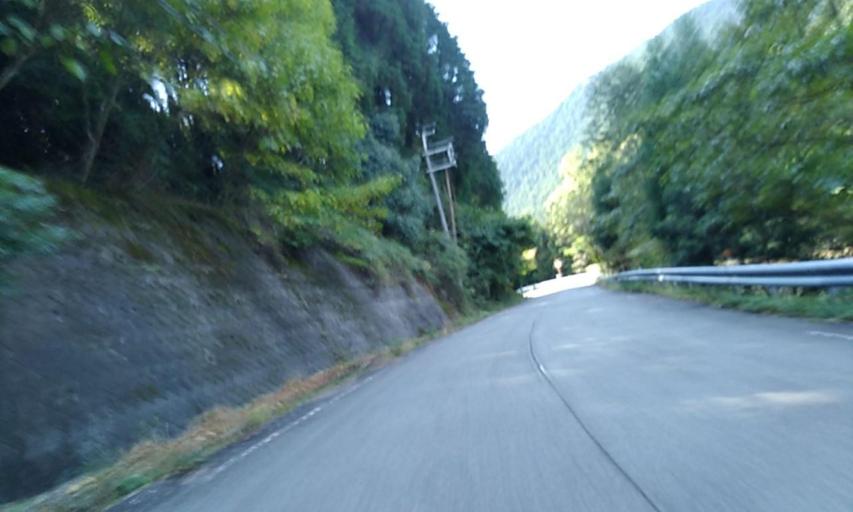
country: JP
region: Wakayama
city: Iwade
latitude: 34.1133
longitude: 135.3450
